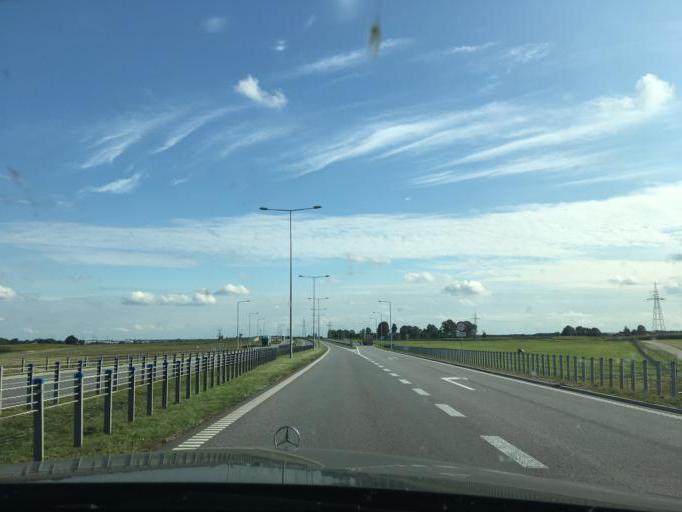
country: PL
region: Podlasie
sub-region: Powiat augustowski
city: Augustow
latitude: 53.8727
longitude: 22.8836
